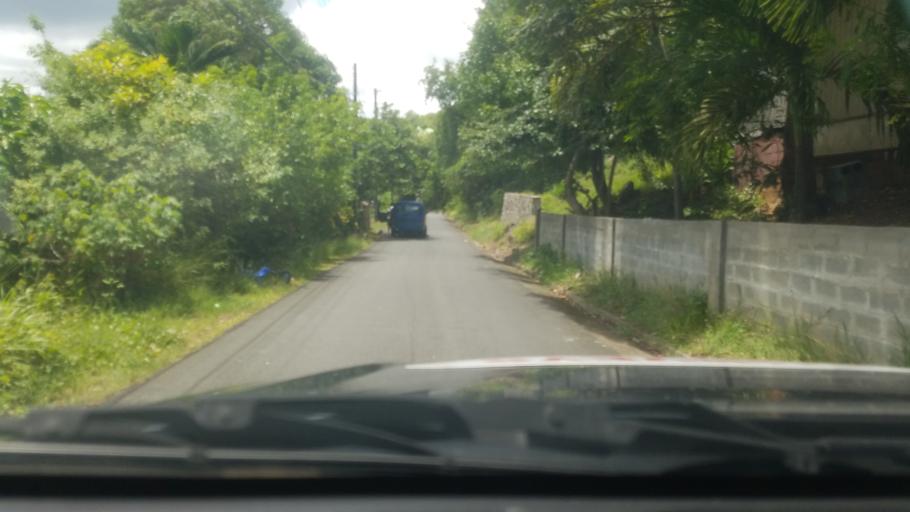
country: LC
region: Dennery Quarter
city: Dennery
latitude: 13.9159
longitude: -60.8934
